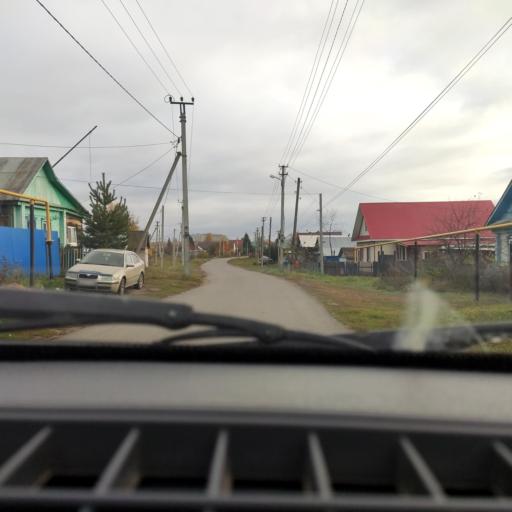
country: RU
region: Bashkortostan
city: Avdon
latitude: 54.6421
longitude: 55.7403
